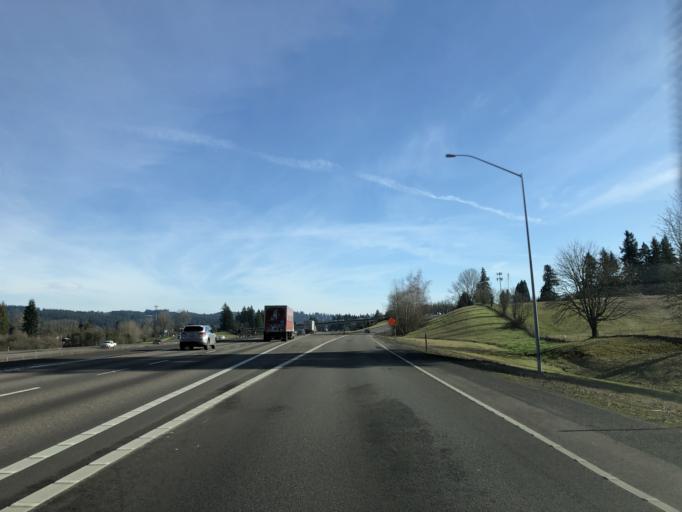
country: US
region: Oregon
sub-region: Clackamas County
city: Stafford
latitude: 45.3716
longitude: -122.7125
